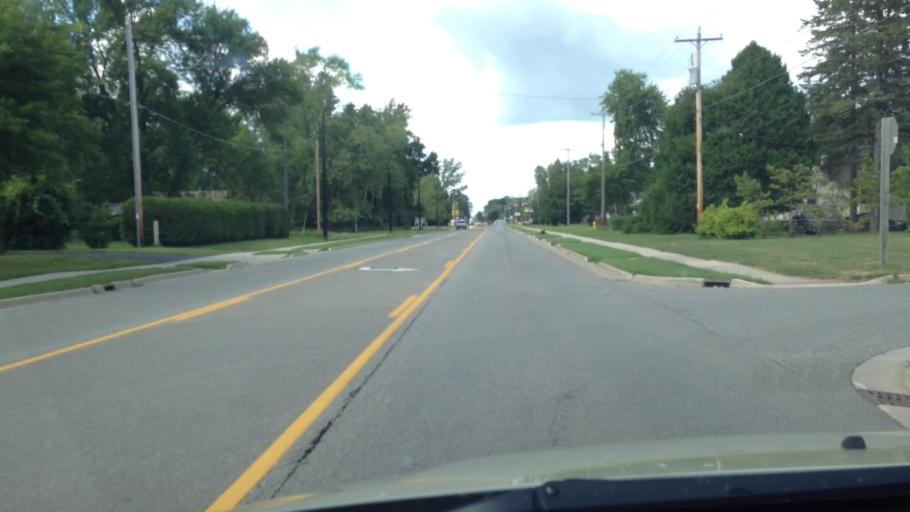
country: US
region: Michigan
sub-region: Menominee County
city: Menominee
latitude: 45.1404
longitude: -87.6121
